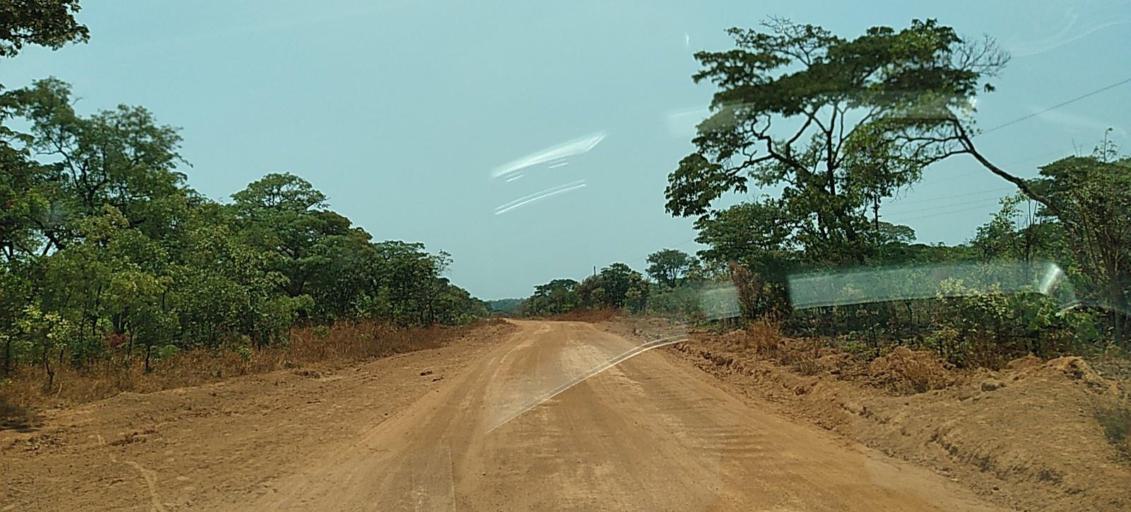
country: CD
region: Katanga
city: Kipushi
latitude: -11.9257
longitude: 27.0030
